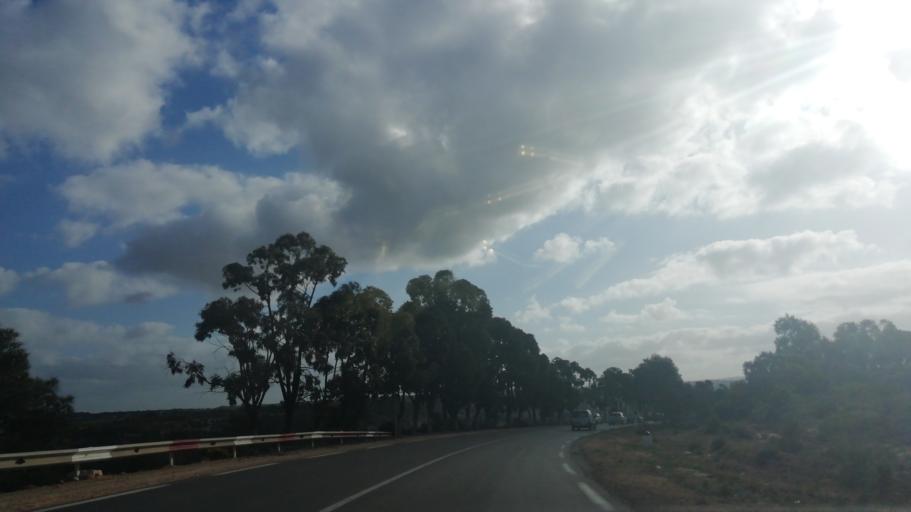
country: DZ
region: Relizane
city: Mazouna
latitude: 36.2394
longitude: 0.5289
